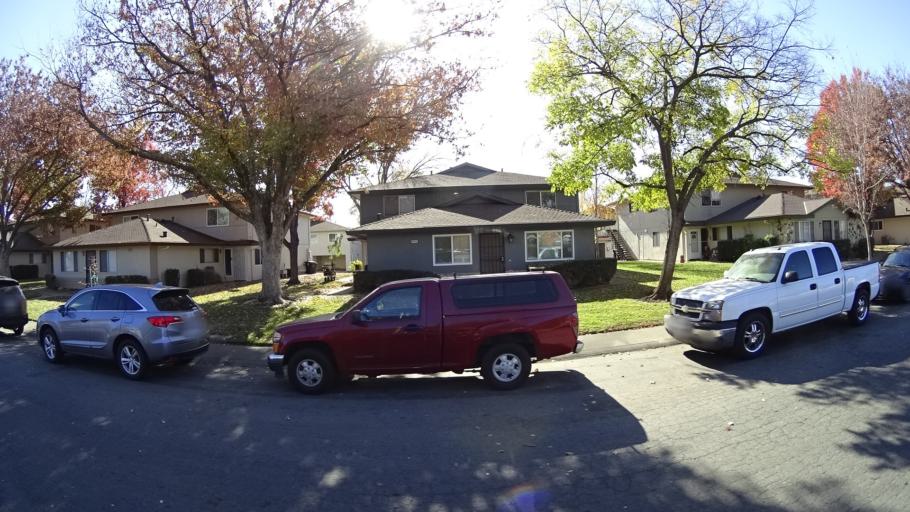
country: US
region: California
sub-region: Sacramento County
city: Antelope
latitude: 38.6790
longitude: -121.3123
